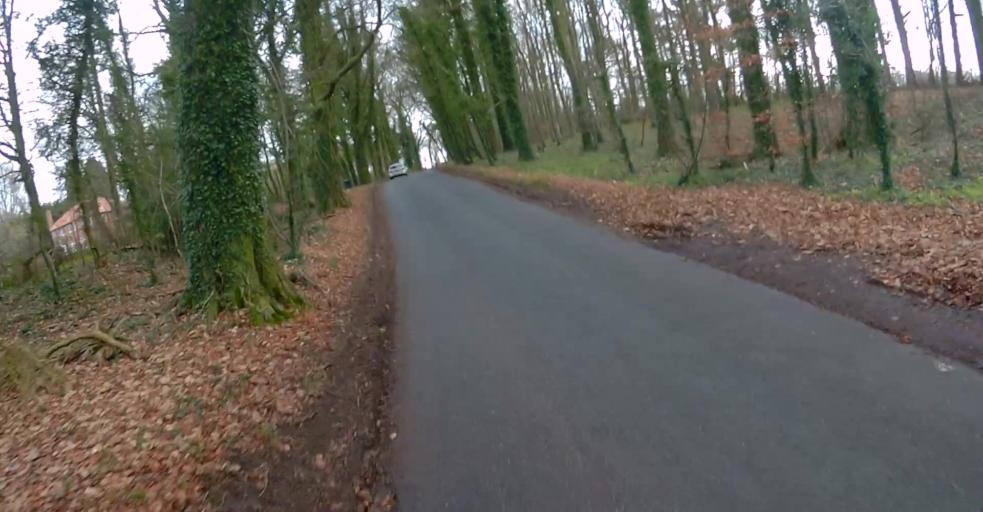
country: GB
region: England
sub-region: Hampshire
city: Basingstoke
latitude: 51.2225
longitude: -1.1217
